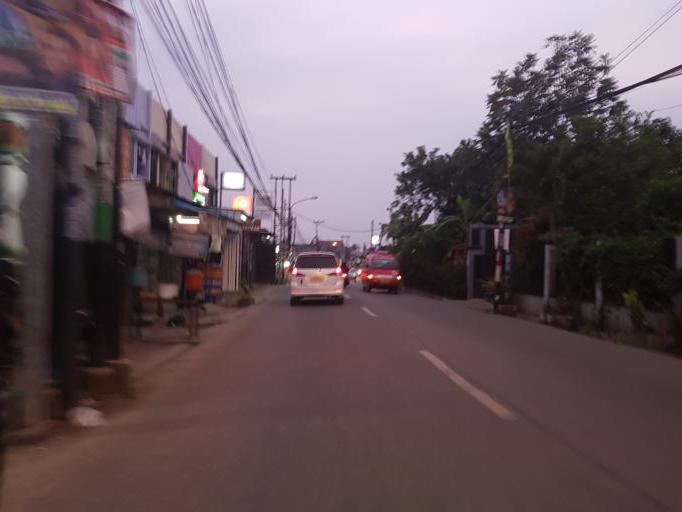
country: ID
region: West Java
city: Bekasi
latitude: -6.2939
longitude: 106.9196
